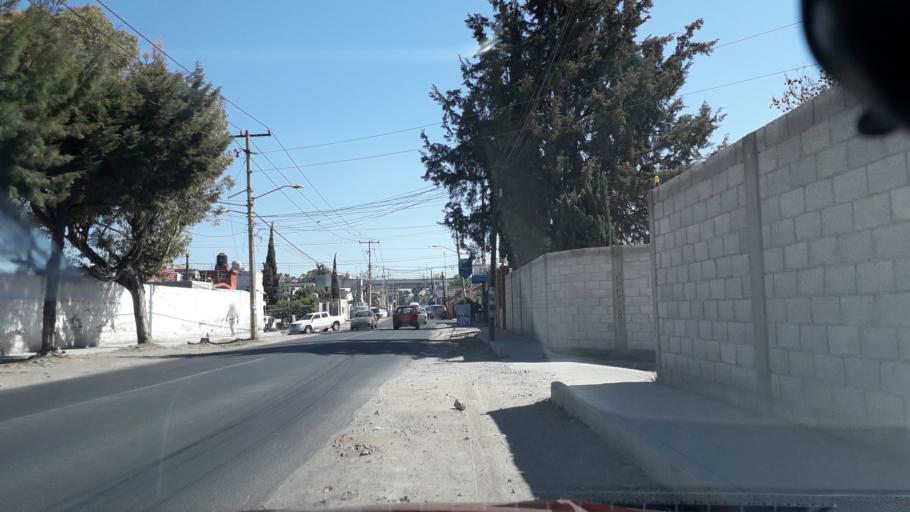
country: MX
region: Puebla
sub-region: Cuautlancingo
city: Sanctorum
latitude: 19.0856
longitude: -98.2144
